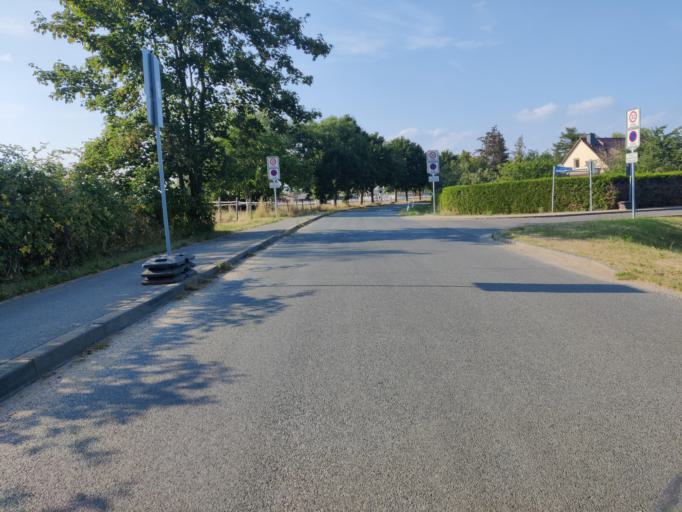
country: DE
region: Saxony
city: Neukieritzsch
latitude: 51.1649
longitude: 12.4327
